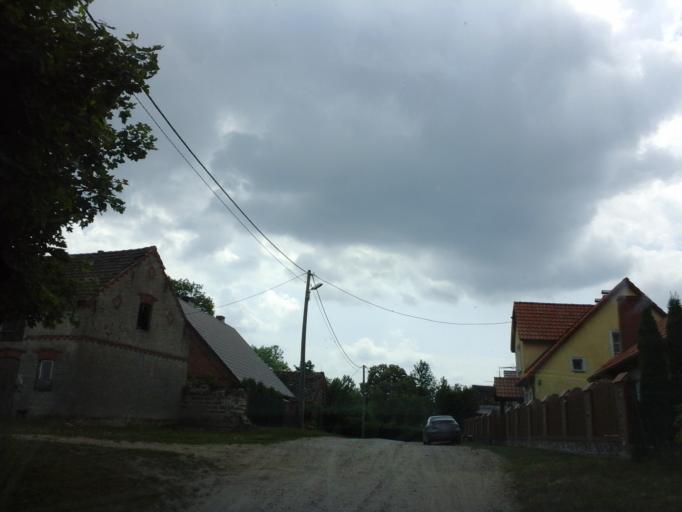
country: PL
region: West Pomeranian Voivodeship
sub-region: Powiat walecki
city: Miroslawiec
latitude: 53.2521
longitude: 16.0209
